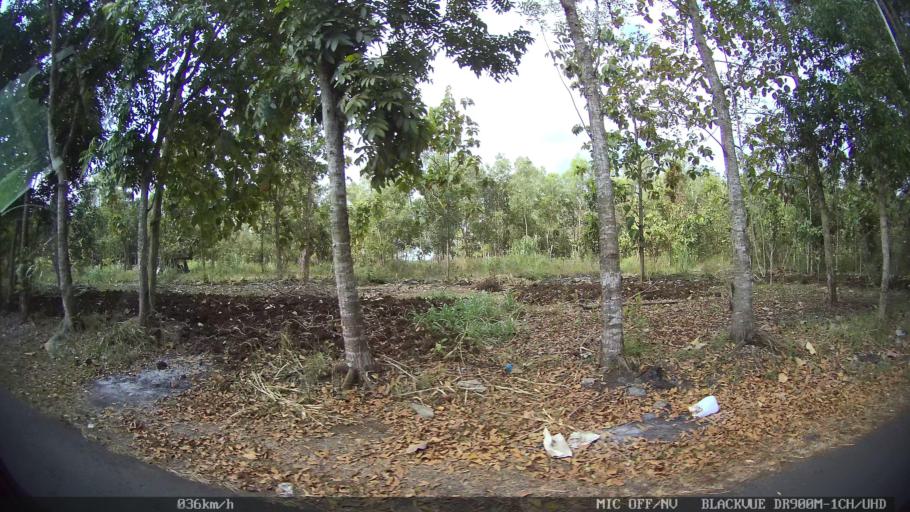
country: ID
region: Daerah Istimewa Yogyakarta
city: Bantul
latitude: -7.8612
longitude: 110.3062
